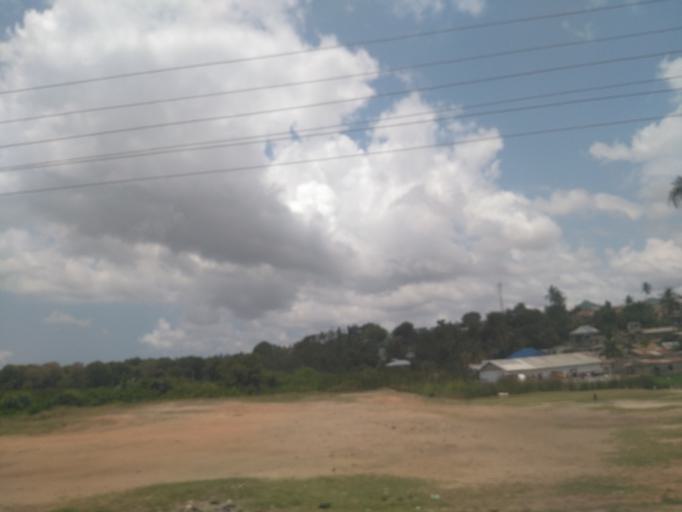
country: TZ
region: Dar es Salaam
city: Dar es Salaam
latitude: -6.8833
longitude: 39.2689
